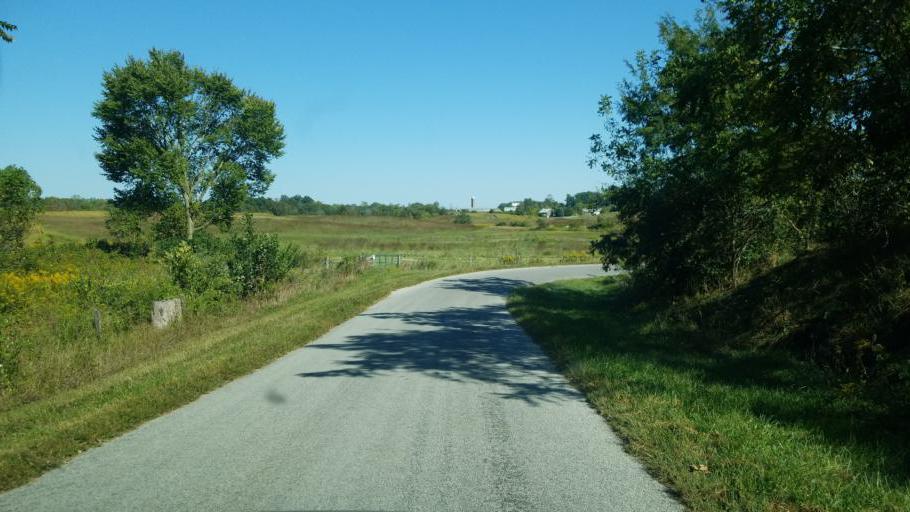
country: US
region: Ohio
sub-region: Champaign County
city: Mechanicsburg
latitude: 40.1163
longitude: -83.5990
